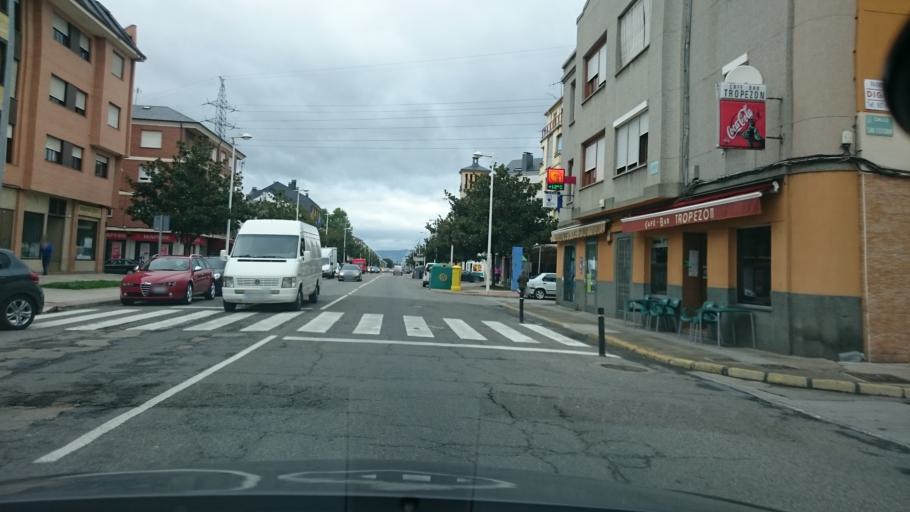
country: ES
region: Castille and Leon
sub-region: Provincia de Leon
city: Ponferrada
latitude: 42.5585
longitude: -6.6210
